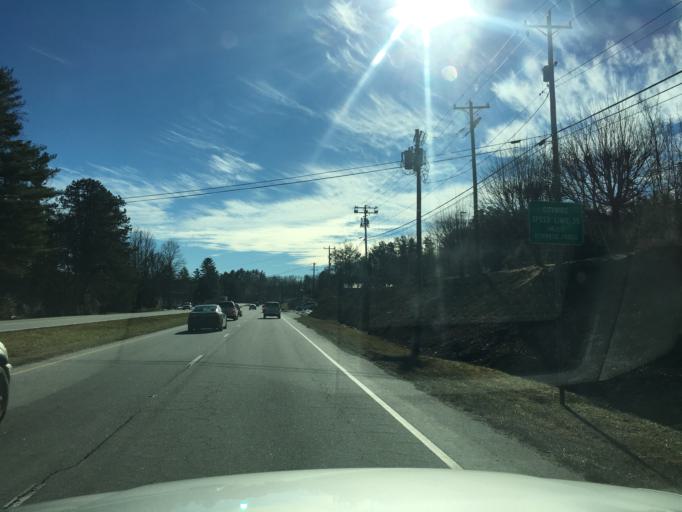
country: US
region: North Carolina
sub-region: Transylvania County
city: Brevard
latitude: 35.2623
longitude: -82.7157
